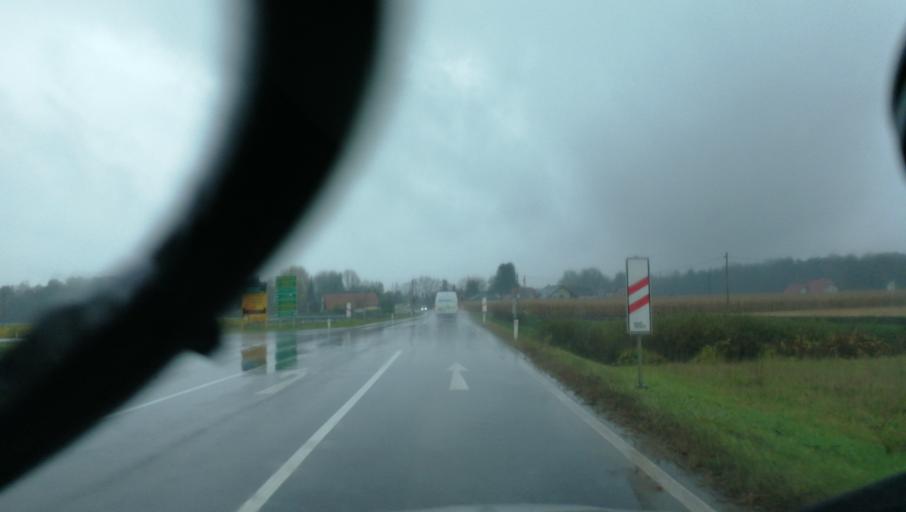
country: AT
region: Styria
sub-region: Politischer Bezirk Leibnitz
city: Spielfeld
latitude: 46.7189
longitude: 15.6575
